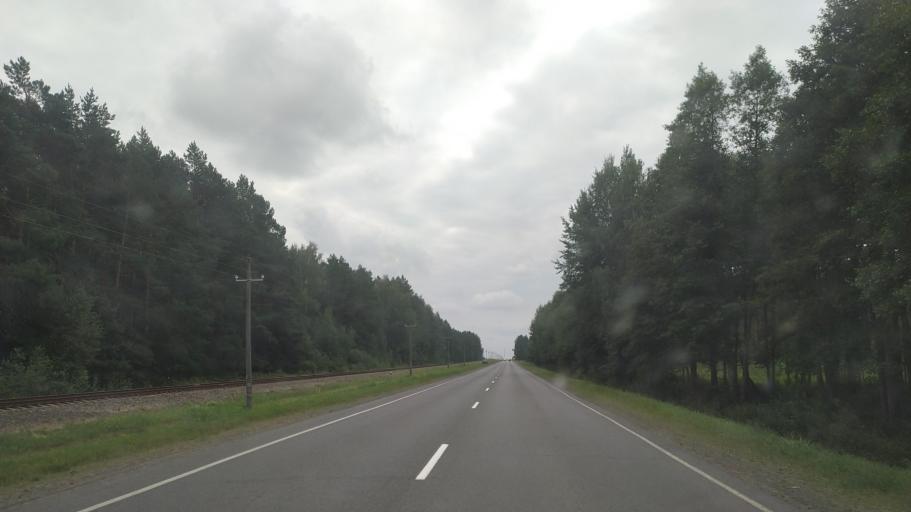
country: BY
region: Brest
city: Byelaazyorsk
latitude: 52.5287
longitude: 25.1454
